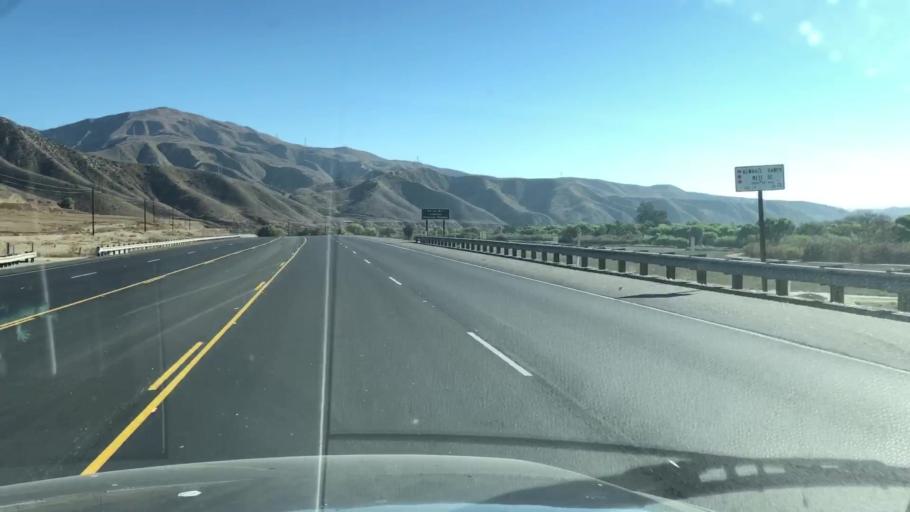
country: US
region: California
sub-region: Ventura County
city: Piru
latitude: 34.4067
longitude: -118.7384
